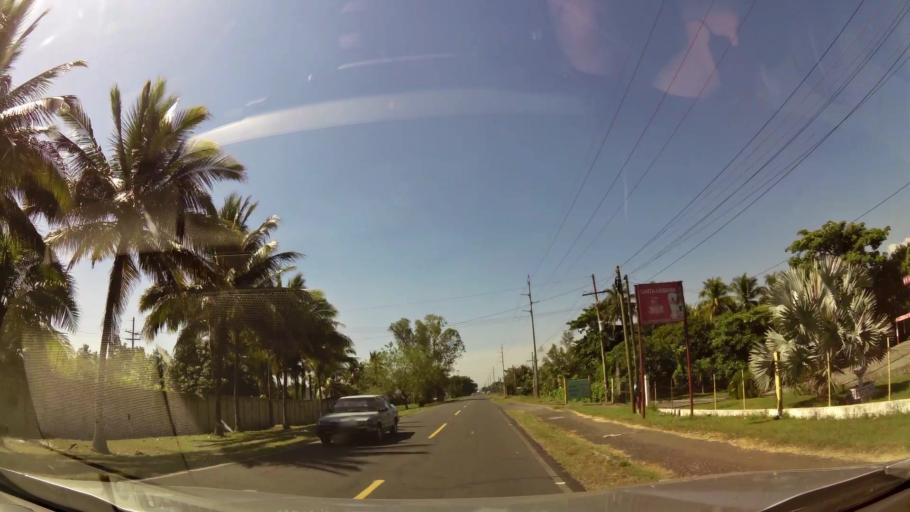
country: GT
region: Escuintla
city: Puerto San Jose
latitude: 13.9328
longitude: -90.7703
